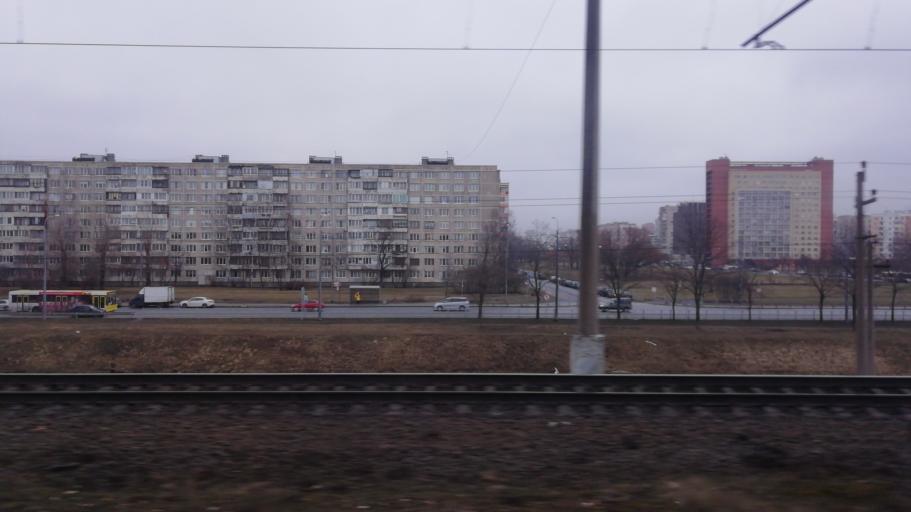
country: RU
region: St.-Petersburg
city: Kupchino
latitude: 59.8670
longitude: 30.3579
